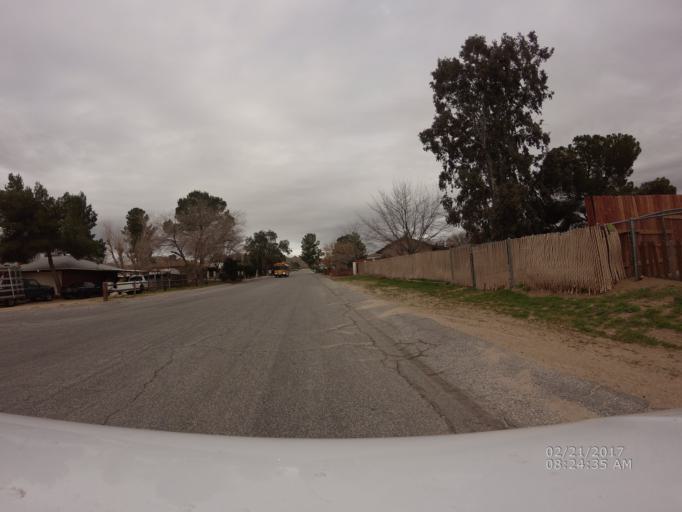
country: US
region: California
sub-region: Los Angeles County
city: Lake Los Angeles
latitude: 34.5982
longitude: -117.8395
